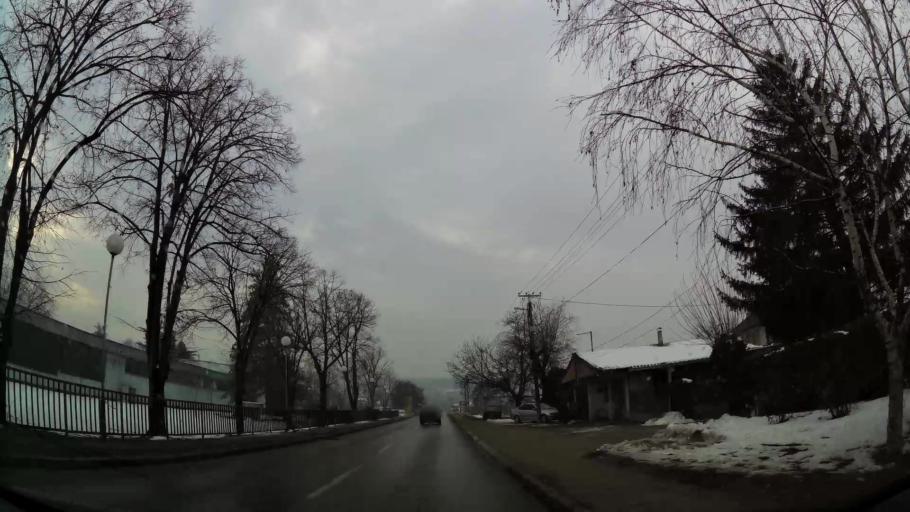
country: MK
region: Saraj
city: Saraj
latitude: 42.0262
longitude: 21.3519
